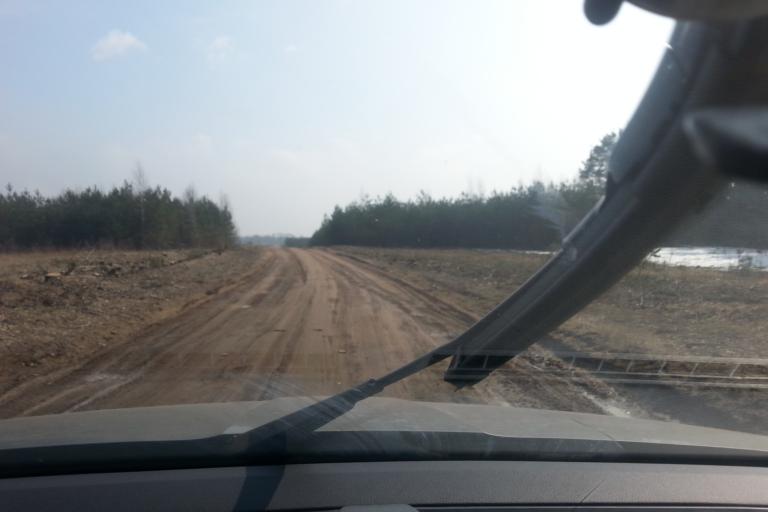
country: LT
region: Vilnius County
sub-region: Trakai
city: Rudiskes
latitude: 54.5017
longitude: 24.9610
